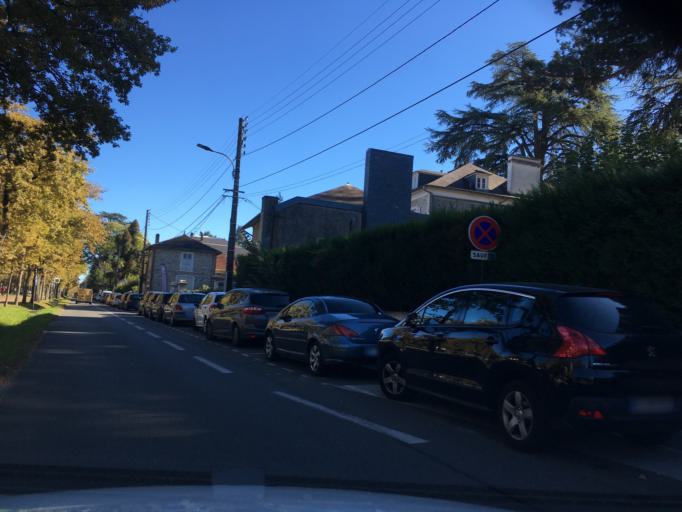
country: FR
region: Aquitaine
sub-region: Departement des Pyrenees-Atlantiques
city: Pau
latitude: 43.3034
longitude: -0.3513
